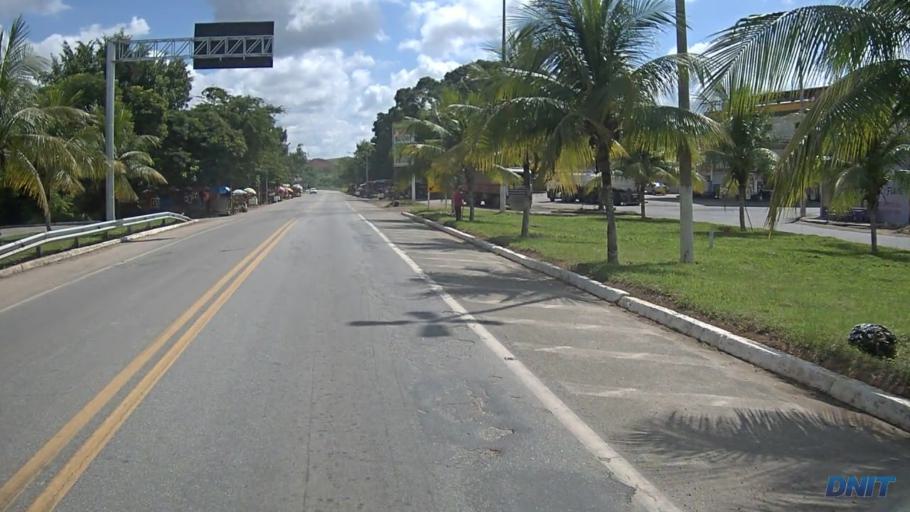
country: BR
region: Minas Gerais
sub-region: Belo Oriente
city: Belo Oriente
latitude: -19.1549
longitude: -42.2364
